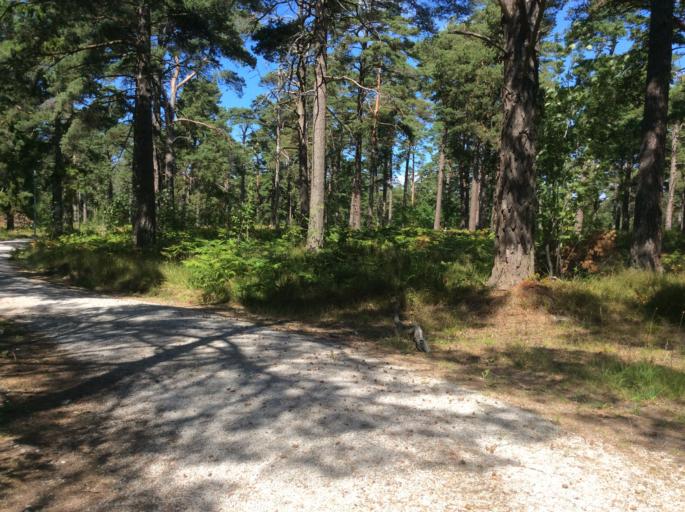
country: SE
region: Gotland
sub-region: Gotland
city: Vibble
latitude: 57.6011
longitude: 18.2786
